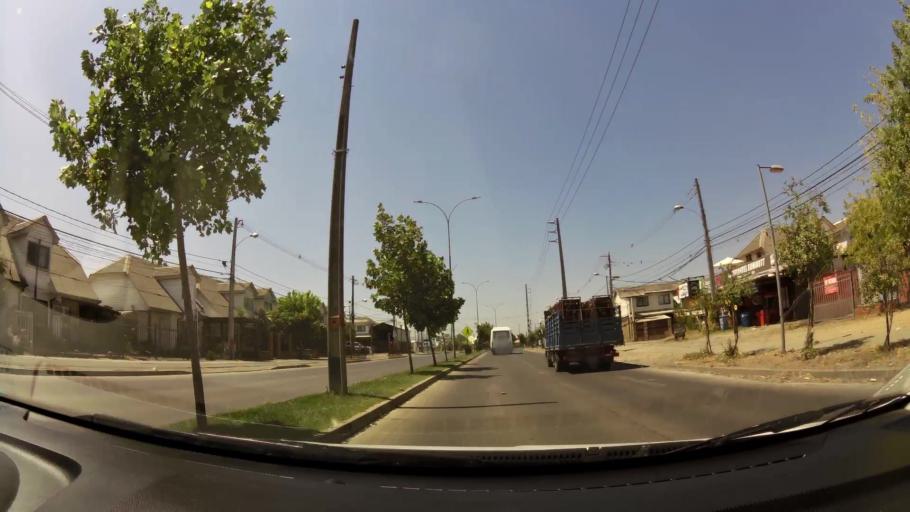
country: CL
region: Maule
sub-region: Provincia de Talca
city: Talca
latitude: -35.4387
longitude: -71.6377
